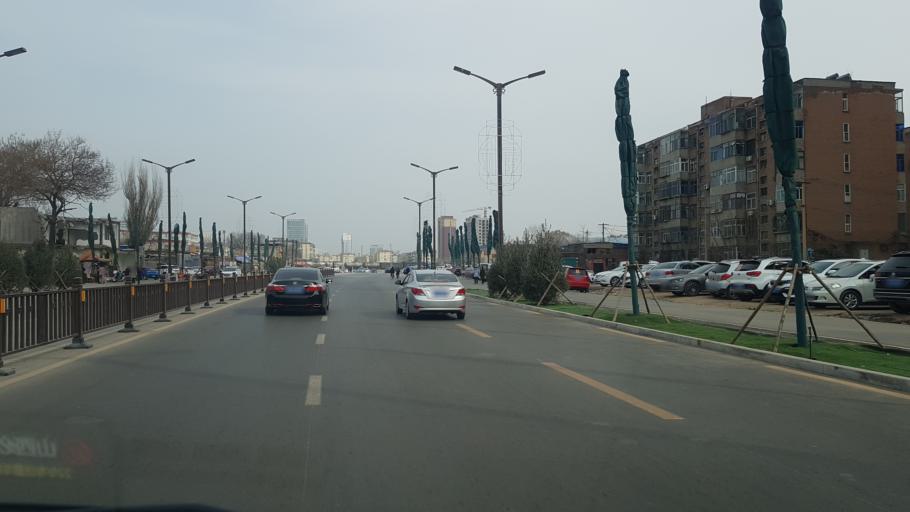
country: CN
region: Shanxi Sheng
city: Yuci
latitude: 37.6901
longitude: 112.7264
